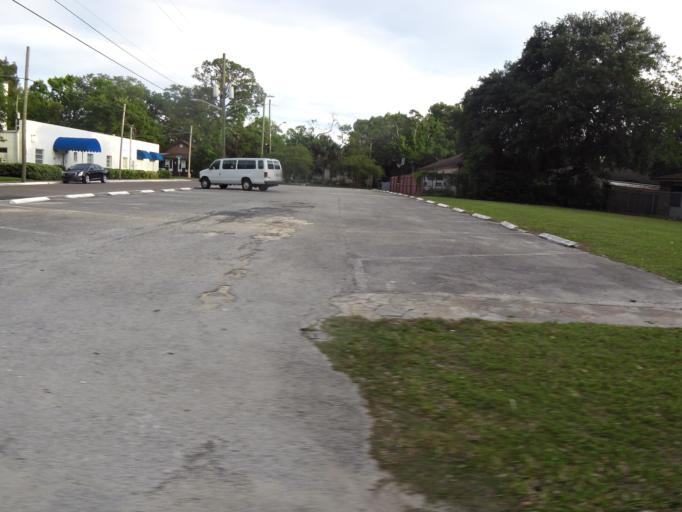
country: US
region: Florida
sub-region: Duval County
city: Jacksonville
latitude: 30.3535
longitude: -81.6391
